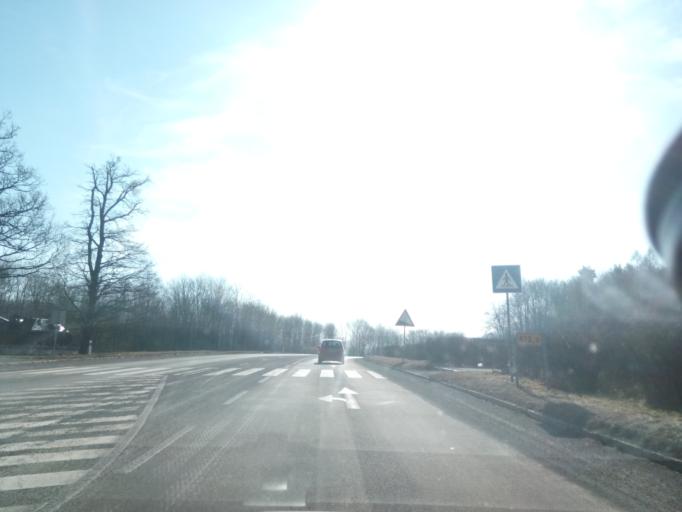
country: SK
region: Kosicky
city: Secovce
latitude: 48.7394
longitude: 21.5348
